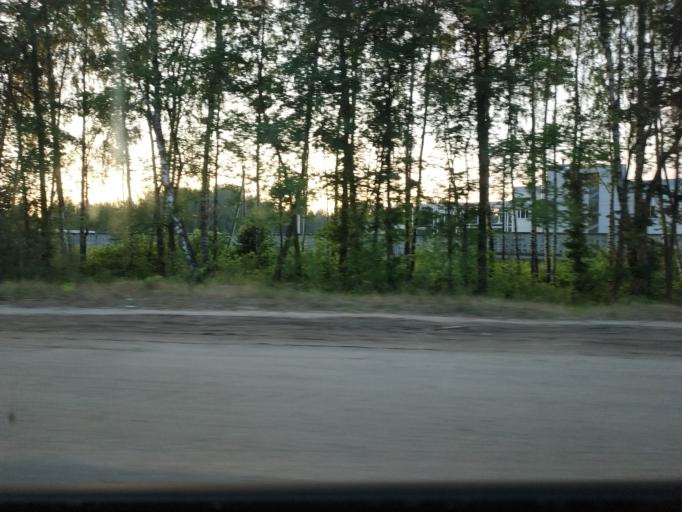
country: RU
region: Moskovskaya
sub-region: Shchelkovskiy Rayon
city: Grebnevo
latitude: 55.9733
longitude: 38.0935
